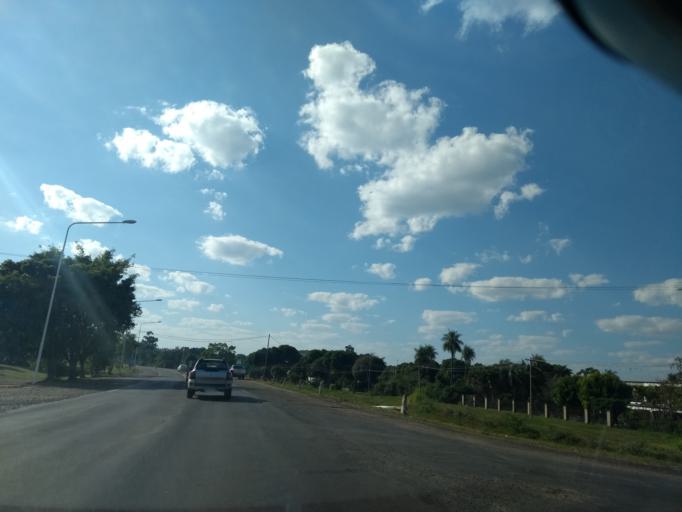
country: AR
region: Corrientes
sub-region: Departamento de San Cosme
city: San Cosme
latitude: -27.3905
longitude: -58.5536
